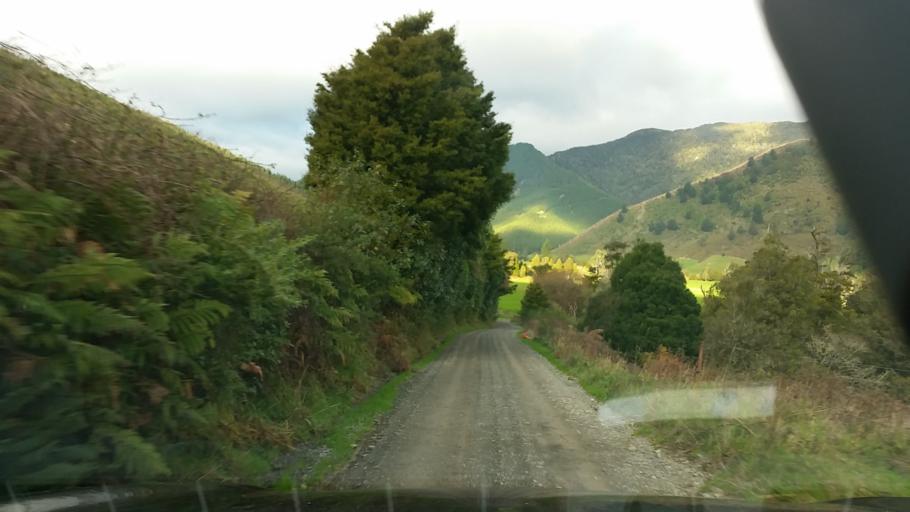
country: NZ
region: Nelson
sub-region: Nelson City
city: Nelson
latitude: -41.2083
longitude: 173.6408
